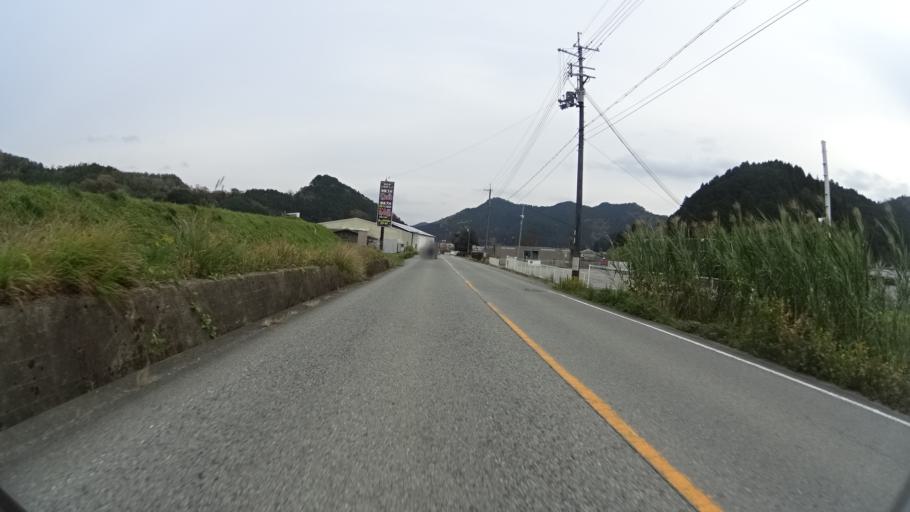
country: JP
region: Hyogo
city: Sasayama
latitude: 35.1027
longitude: 135.1297
